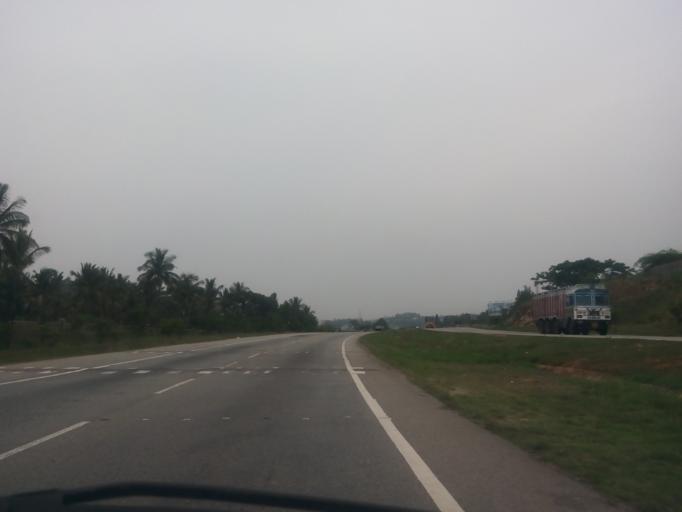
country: IN
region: Karnataka
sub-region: Bangalore Urban
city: Bangalore
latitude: 12.8533
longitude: 77.5951
